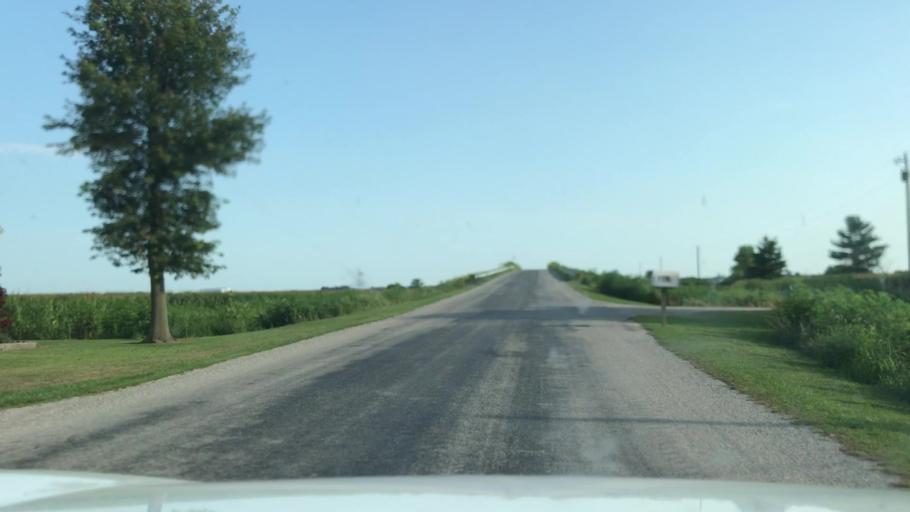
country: US
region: Illinois
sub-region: Washington County
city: Okawville
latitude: 38.4303
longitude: -89.4778
